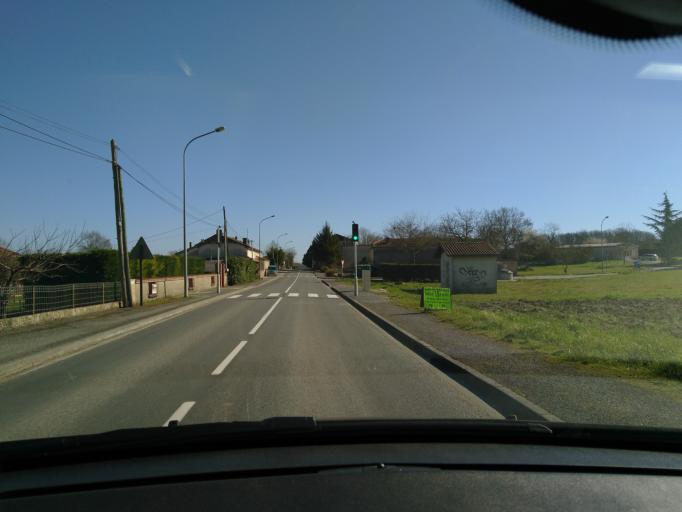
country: FR
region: Aquitaine
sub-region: Departement du Lot-et-Garonne
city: Saint-Hilaire
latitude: 44.5392
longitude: 0.6846
